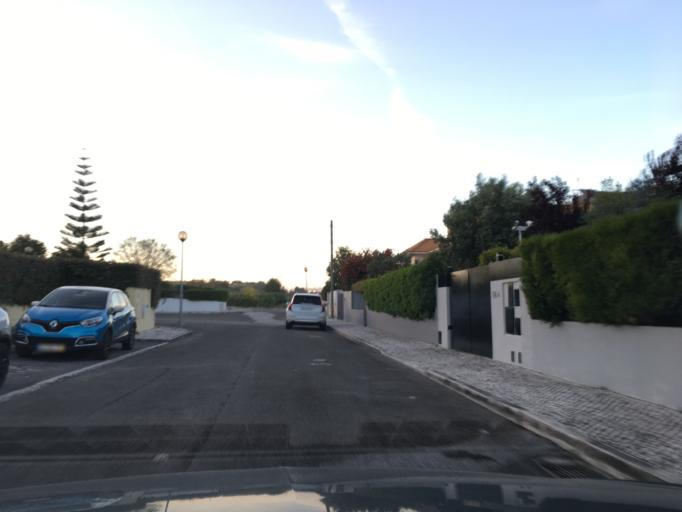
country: PT
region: Lisbon
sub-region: Oeiras
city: Terrugem
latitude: 38.7178
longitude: -9.2813
